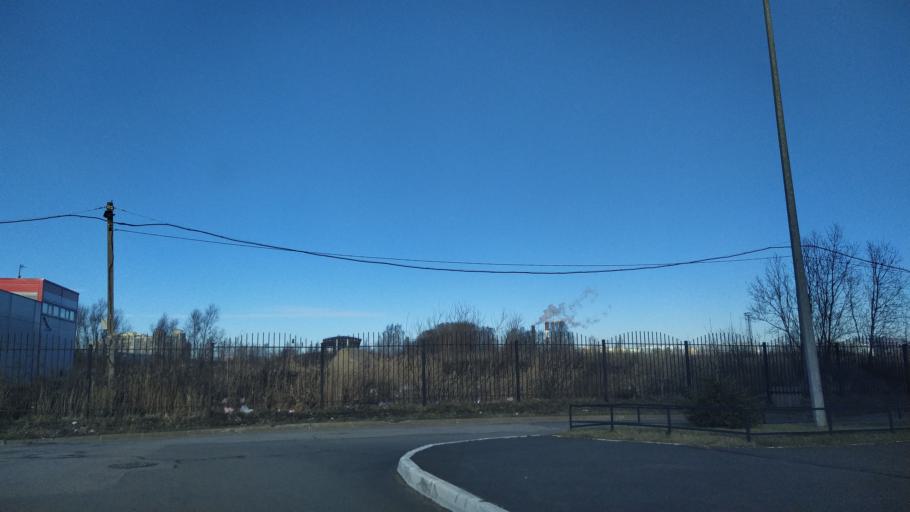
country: RU
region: Leningrad
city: Murino
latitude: 60.0193
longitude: 30.4349
